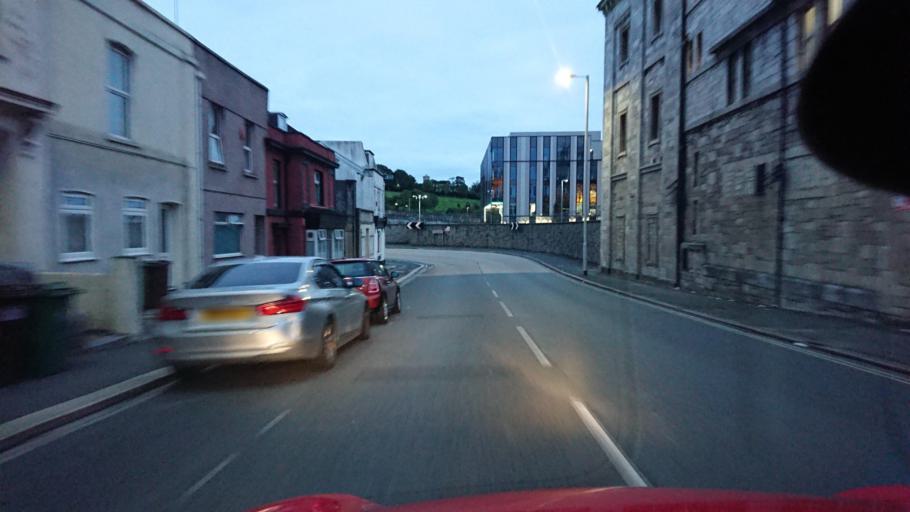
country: GB
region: England
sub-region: Cornwall
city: Millbrook
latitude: 50.3788
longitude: -4.1794
